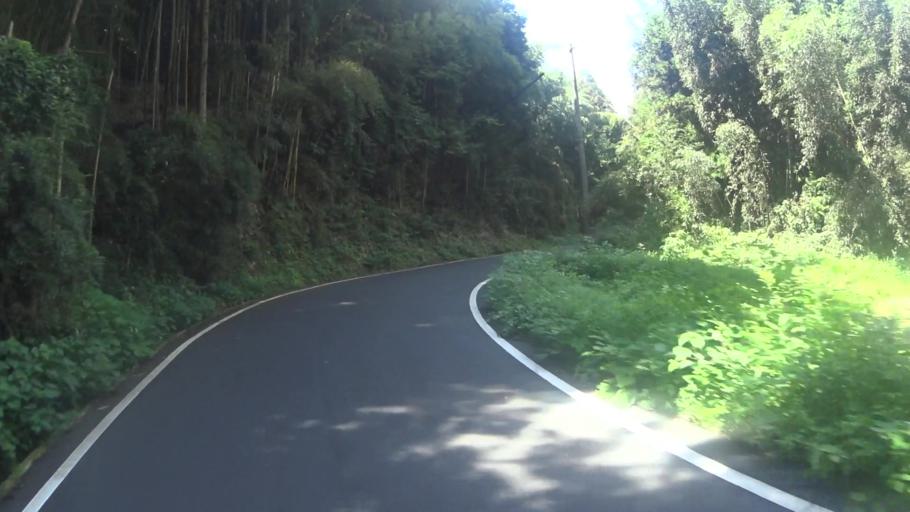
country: JP
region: Nara
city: Nara-shi
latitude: 34.7208
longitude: 135.8829
